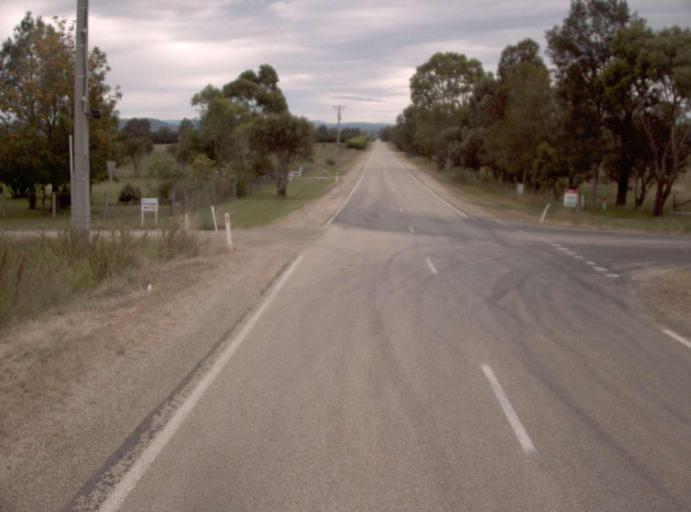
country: AU
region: Victoria
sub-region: East Gippsland
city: Bairnsdale
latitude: -37.8708
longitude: 147.5611
